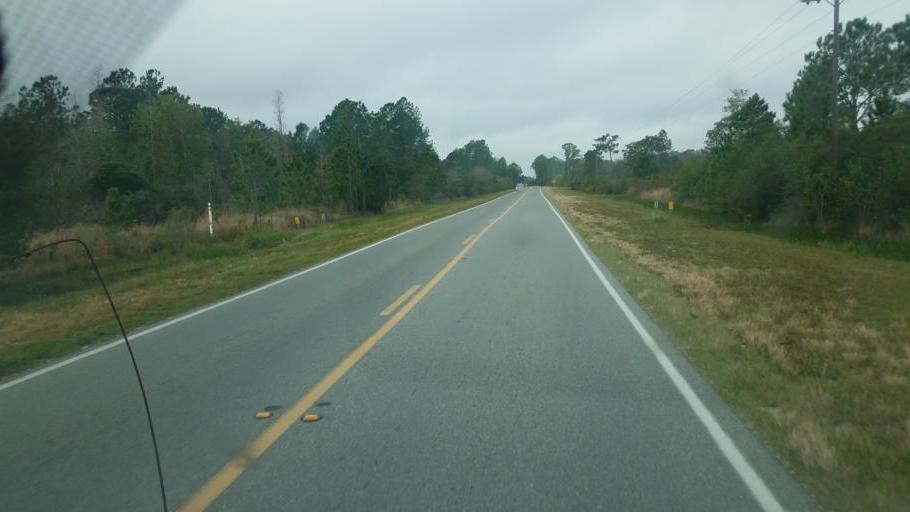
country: US
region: Florida
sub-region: Polk County
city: Polk City
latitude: 28.2588
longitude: -81.7802
